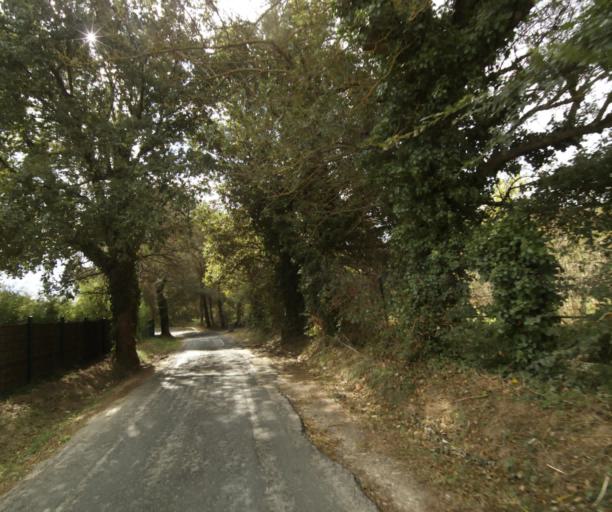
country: FR
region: Languedoc-Roussillon
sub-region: Departement des Pyrenees-Orientales
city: Argelers
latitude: 42.5624
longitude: 3.0316
